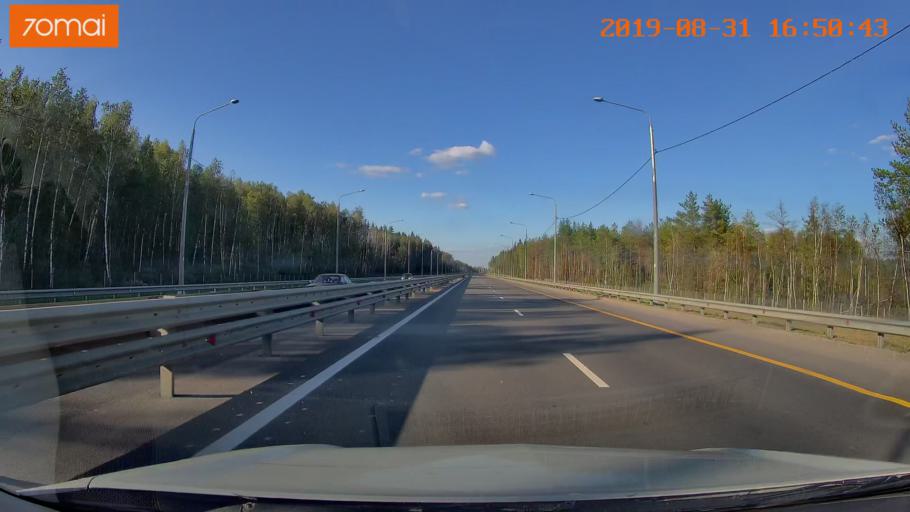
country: RU
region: Kaluga
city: Pyatovskiy
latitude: 54.7137
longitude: 36.1648
